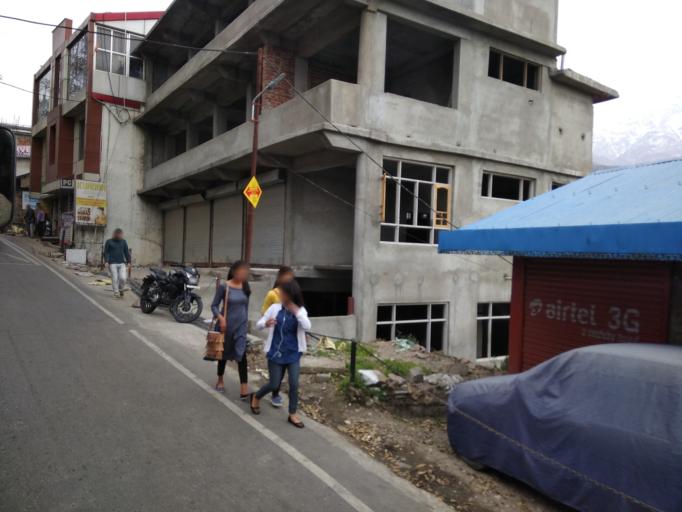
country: IN
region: Himachal Pradesh
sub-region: Kangra
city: Dharmsala
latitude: 32.2062
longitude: 76.3243
